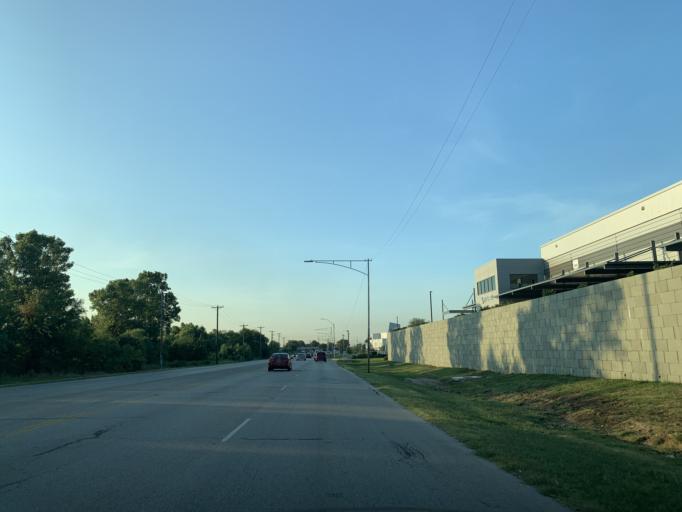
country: US
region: Texas
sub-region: Tarrant County
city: Blue Mound
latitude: 32.8220
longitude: -97.3537
